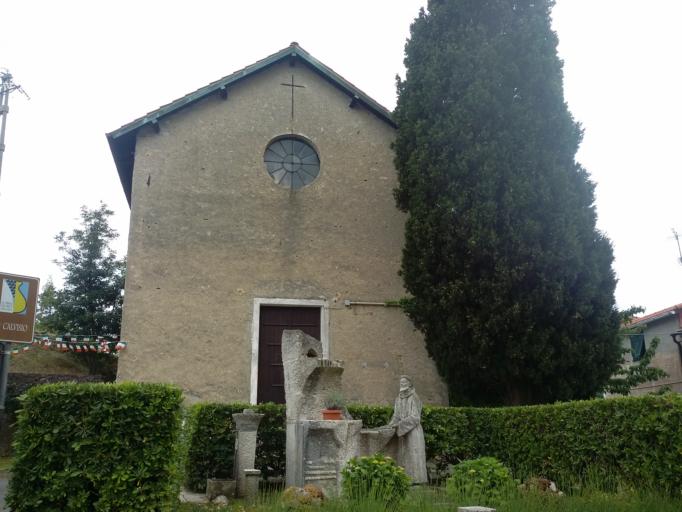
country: IT
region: Liguria
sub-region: Provincia di Savona
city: Orco Feglino
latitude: 44.2222
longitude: 8.3447
